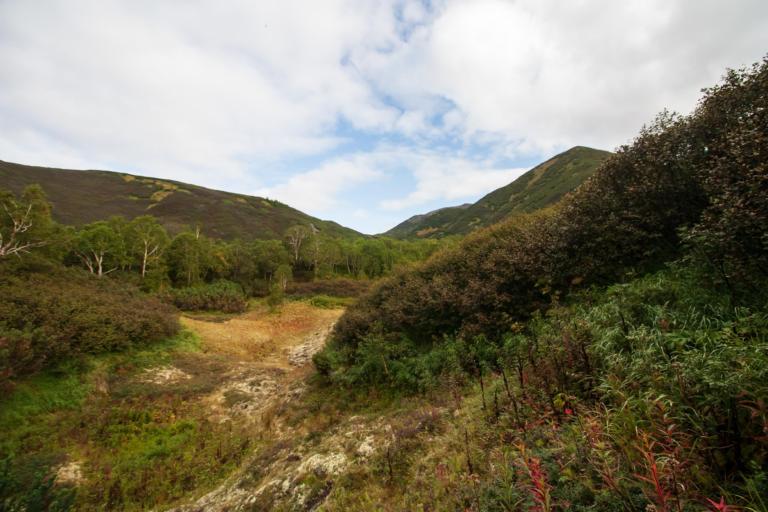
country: RU
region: Kamtsjatka
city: Yelizovo
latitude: 53.8141
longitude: 158.1478
